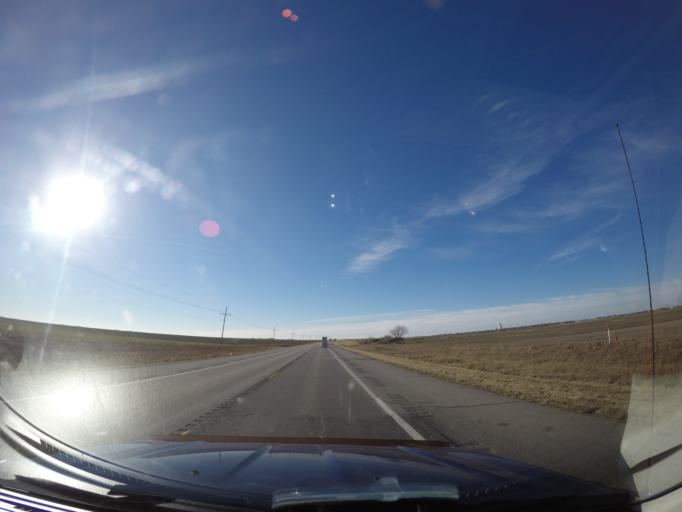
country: US
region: Kansas
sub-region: Marion County
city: Hillsboro
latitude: 38.3621
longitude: -97.2825
